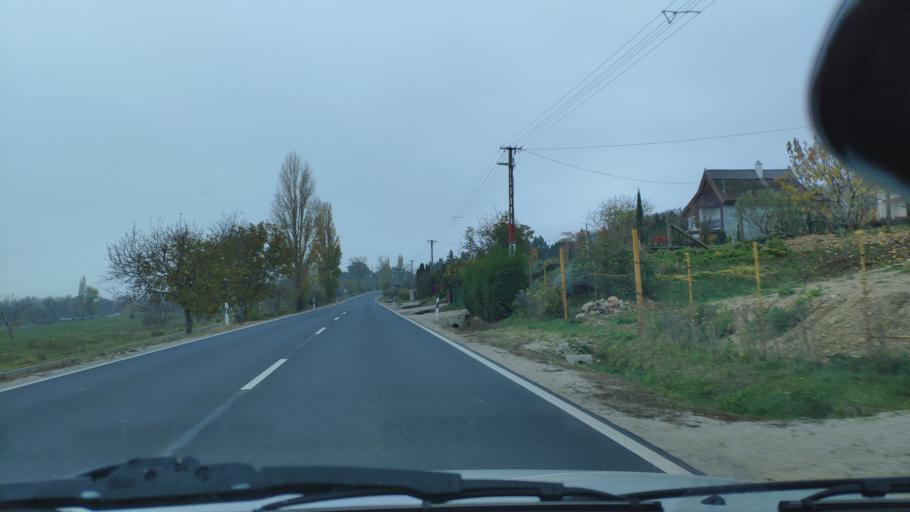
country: HU
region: Zala
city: Vonyarcvashegy
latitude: 46.7749
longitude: 17.3647
